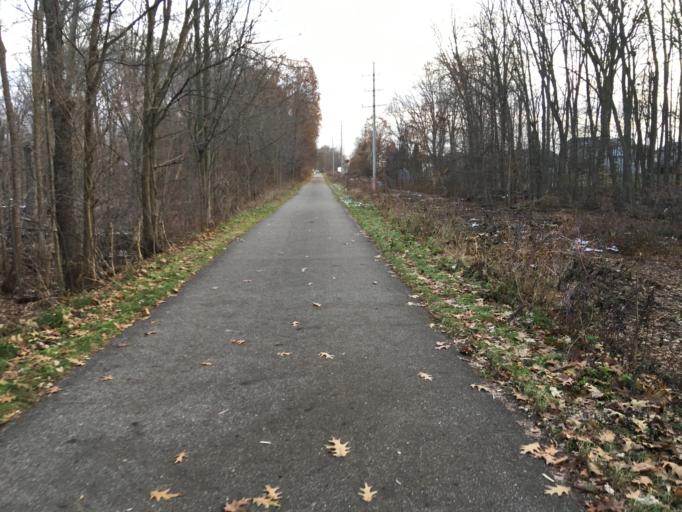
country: US
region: Michigan
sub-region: Kent County
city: Byron Center
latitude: 42.8586
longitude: -85.7332
